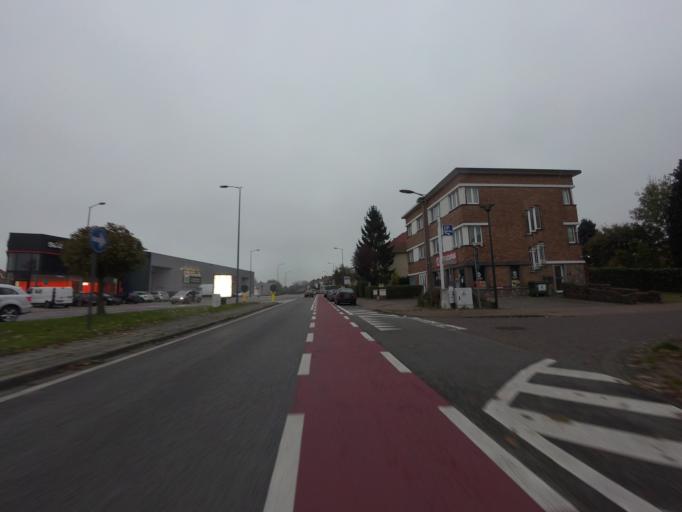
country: BE
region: Flanders
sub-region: Provincie Vlaams-Brabant
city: Diegem
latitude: 50.8636
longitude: 4.4341
